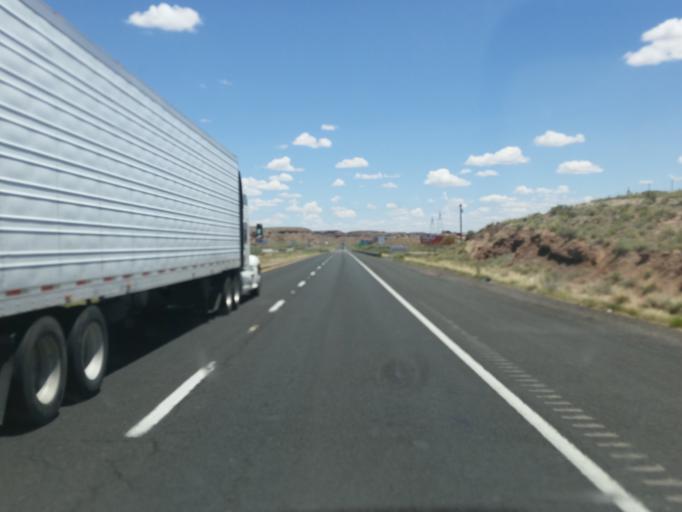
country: US
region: Arizona
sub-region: Navajo County
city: Joseph City
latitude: 34.9478
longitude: -110.2996
